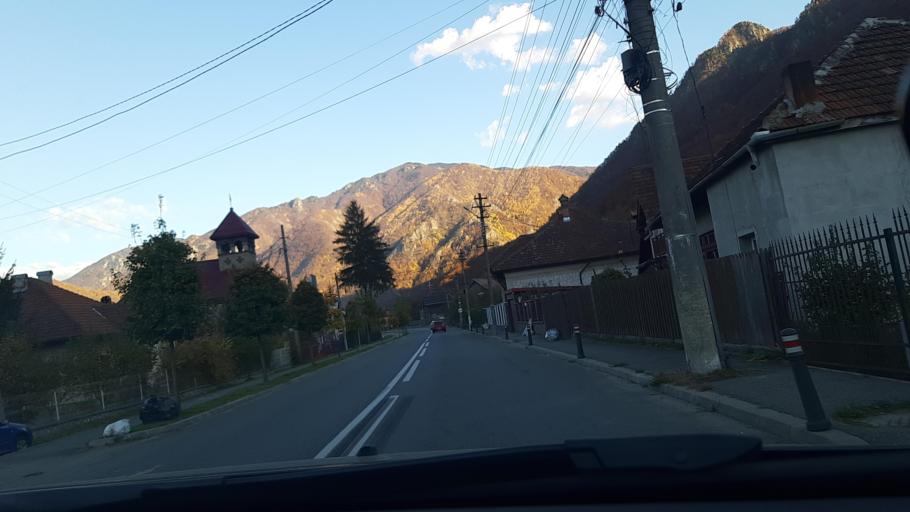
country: RO
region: Valcea
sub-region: Comuna Brezoi
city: Brezoi
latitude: 45.3336
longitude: 24.2556
